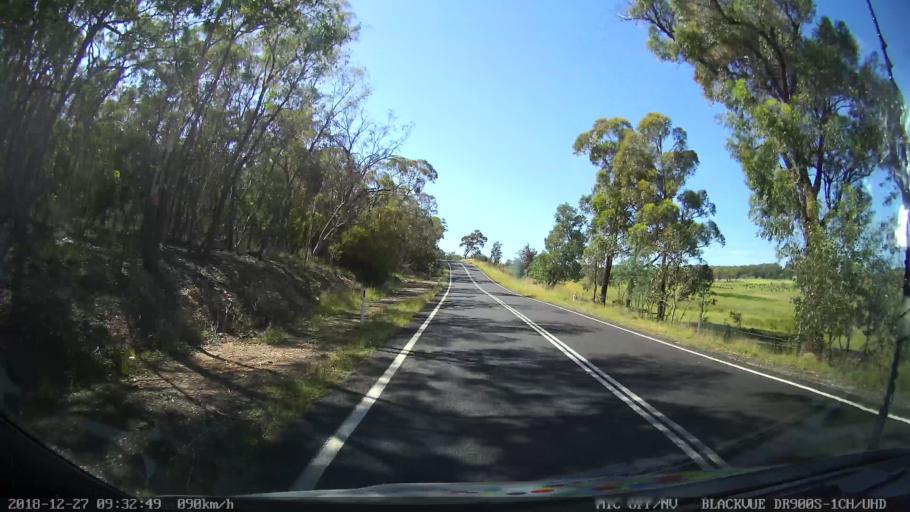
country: AU
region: New South Wales
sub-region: Lithgow
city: Portland
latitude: -33.2122
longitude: 150.0177
